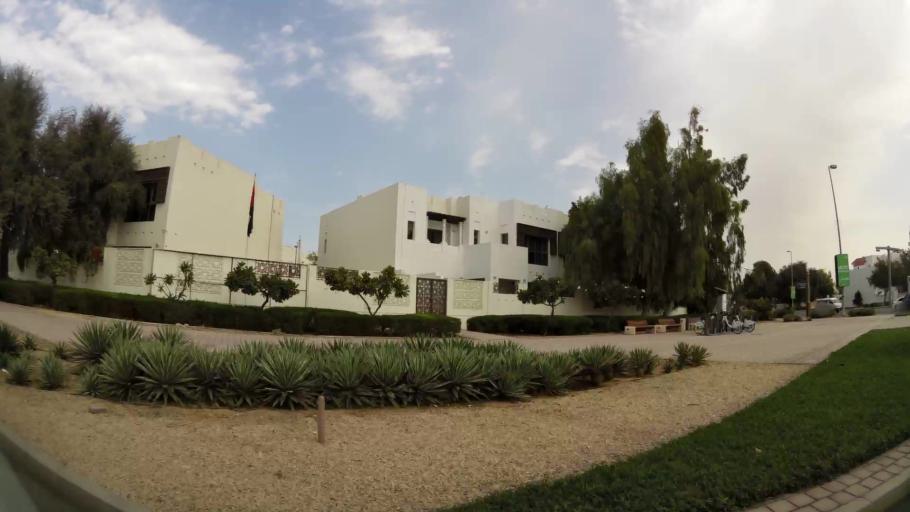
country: AE
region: Abu Dhabi
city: Abu Dhabi
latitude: 24.4543
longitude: 54.3522
